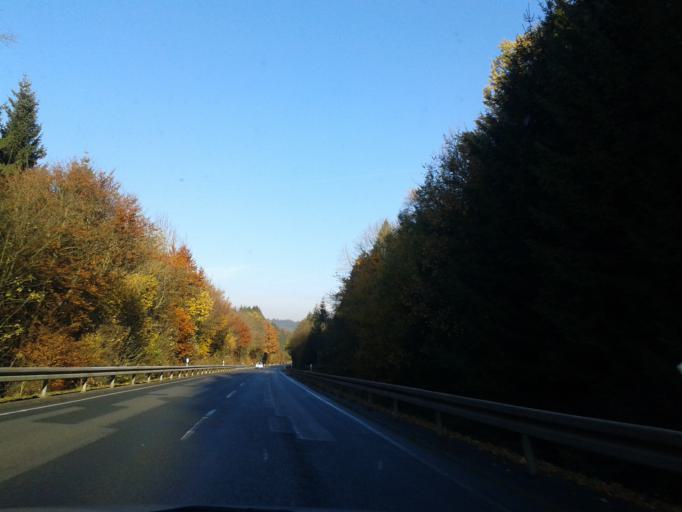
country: DE
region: North Rhine-Westphalia
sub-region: Regierungsbezirk Arnsberg
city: Bestwig
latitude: 51.4232
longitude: 8.4298
